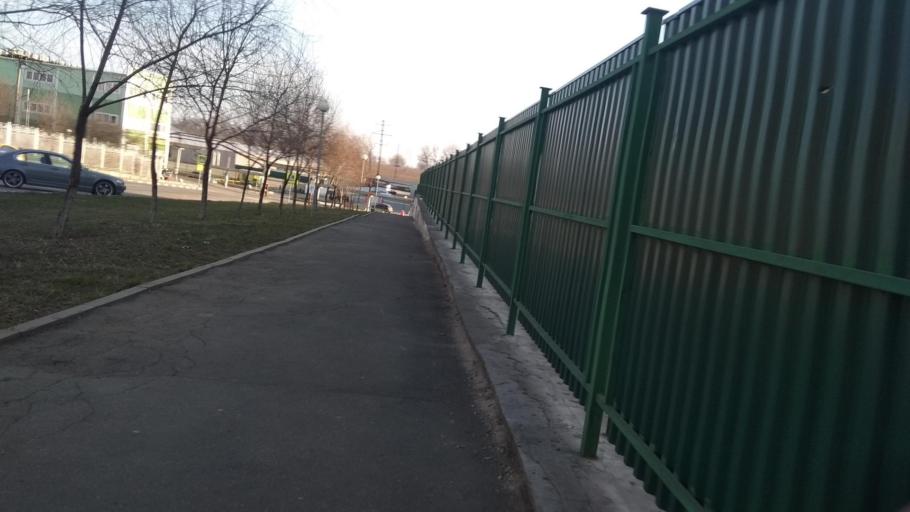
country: RU
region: Moskovskaya
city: Razvilka
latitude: 55.5845
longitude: 37.7269
